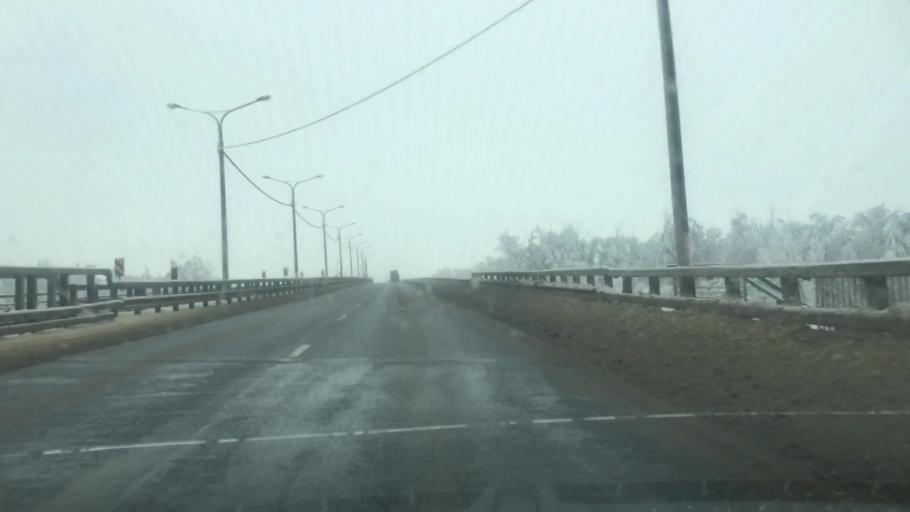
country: RU
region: Lipetsk
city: Yelets
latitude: 52.5491
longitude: 38.7180
